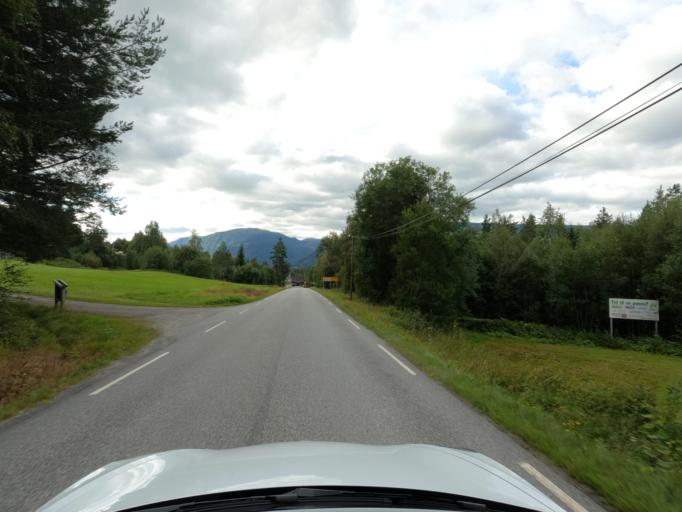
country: NO
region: Telemark
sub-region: Tinn
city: Rjukan
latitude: 59.9977
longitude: 8.8284
